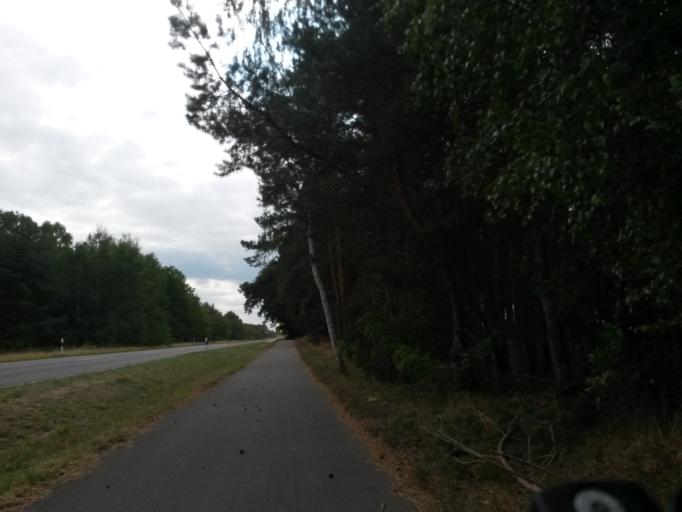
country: DE
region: Saxony-Anhalt
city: Schonhausen
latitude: 52.5557
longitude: 12.0268
